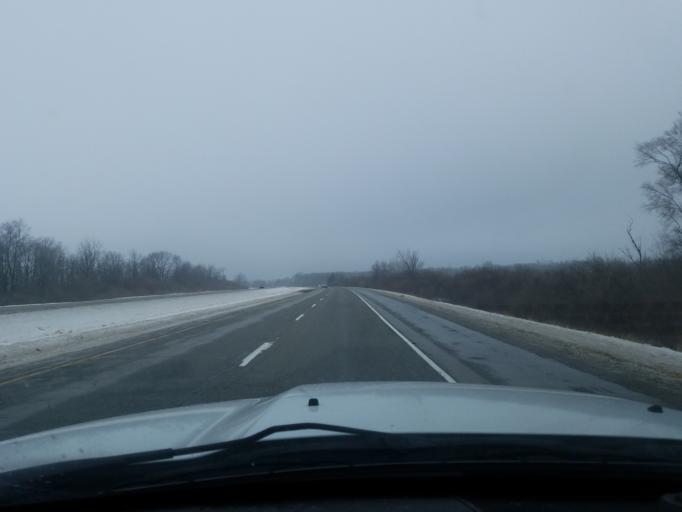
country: US
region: Indiana
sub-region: Fulton County
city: Rochester
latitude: 41.0057
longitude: -86.1675
